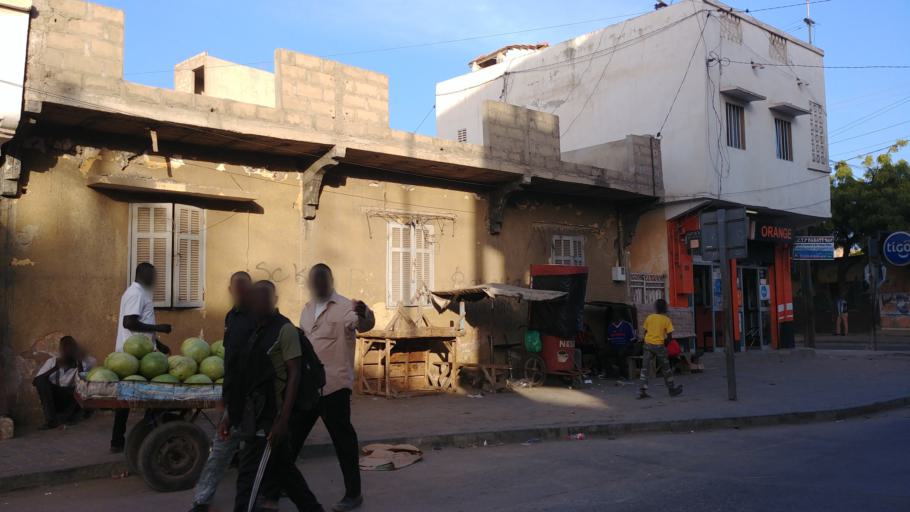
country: SN
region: Saint-Louis
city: Saint-Louis
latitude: 16.0246
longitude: -16.4952
